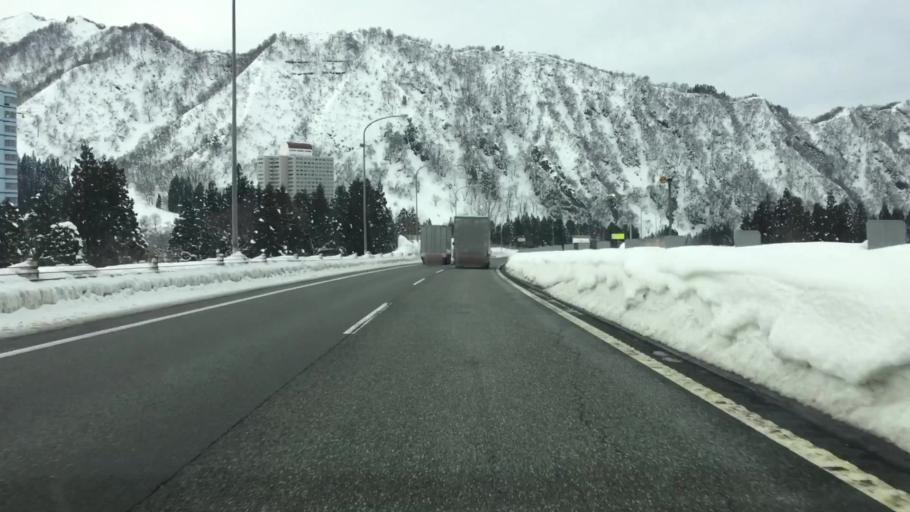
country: JP
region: Niigata
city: Shiozawa
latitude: 36.9073
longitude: 138.8436
